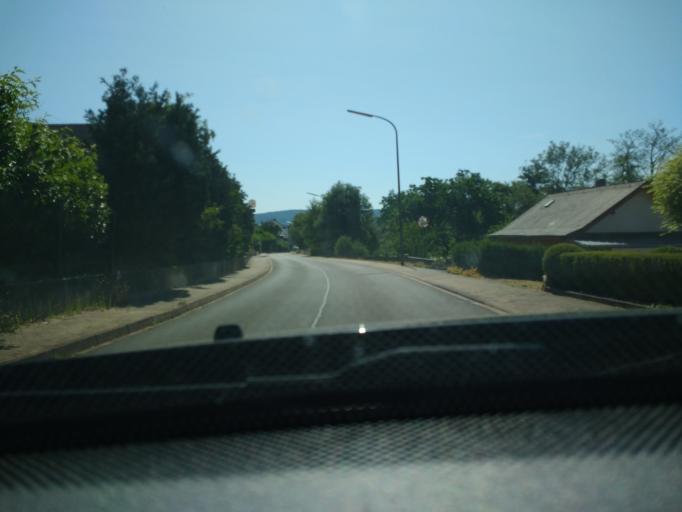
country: DE
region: Rheinland-Pfalz
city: Bausendorf
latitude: 50.0169
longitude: 6.9893
